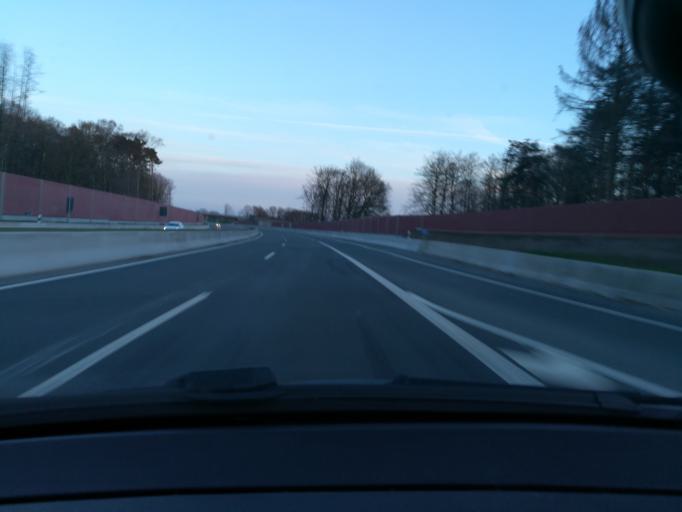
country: DE
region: North Rhine-Westphalia
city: Halle
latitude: 52.0410
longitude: 8.3400
